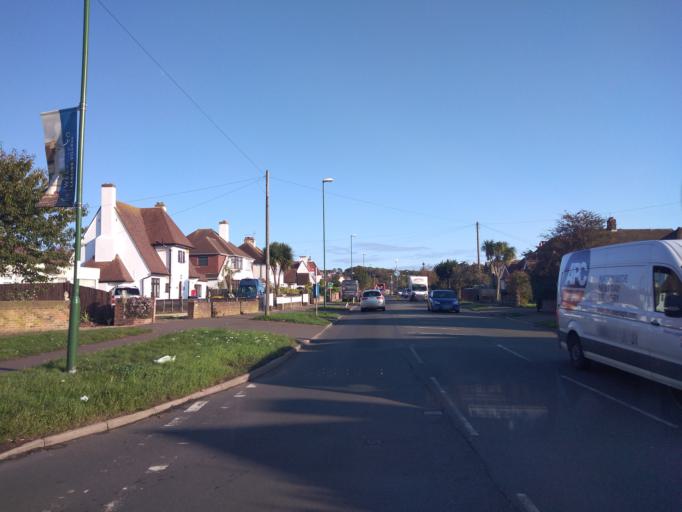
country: GB
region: England
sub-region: West Sussex
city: Lancing
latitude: 50.8316
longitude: -0.3187
